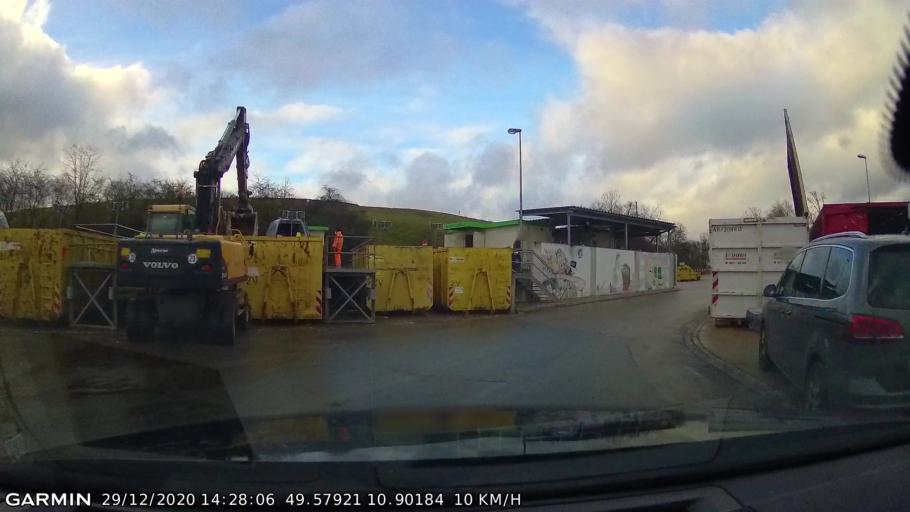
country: DE
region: Bavaria
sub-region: Regierungsbezirk Mittelfranken
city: Herzogenaurach
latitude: 49.5792
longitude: 10.9019
